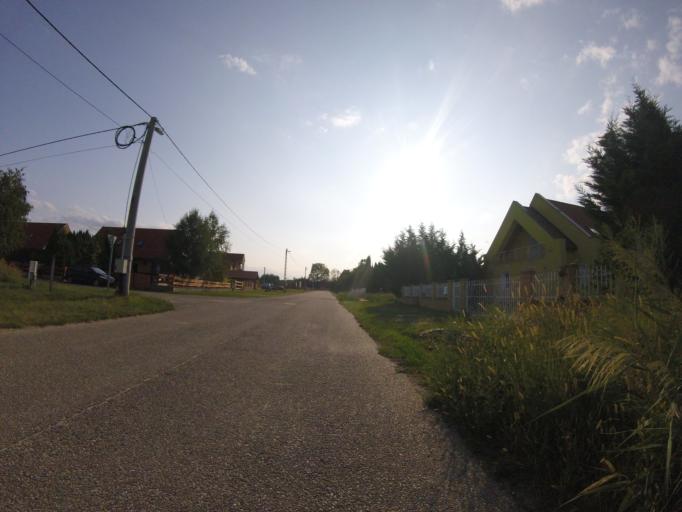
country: HU
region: Gyor-Moson-Sopron
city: Fertod
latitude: 47.6198
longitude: 16.7881
